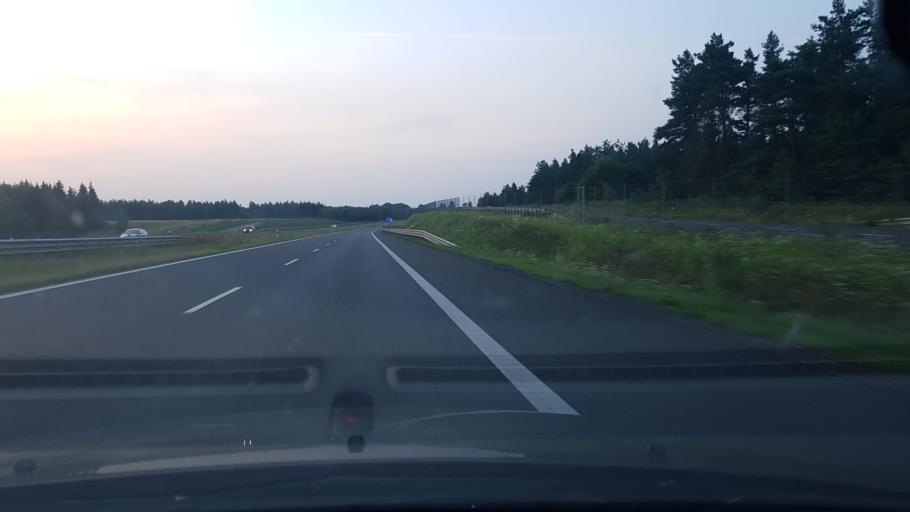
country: PL
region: Warmian-Masurian Voivodeship
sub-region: Powiat olsztynski
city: Olsztynek
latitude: 53.4677
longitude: 20.3217
